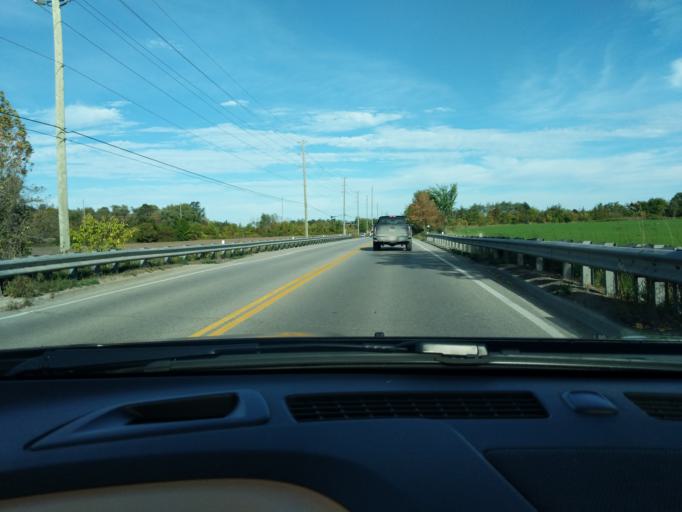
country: CA
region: Ontario
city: Collingwood
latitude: 44.4815
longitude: -80.2006
